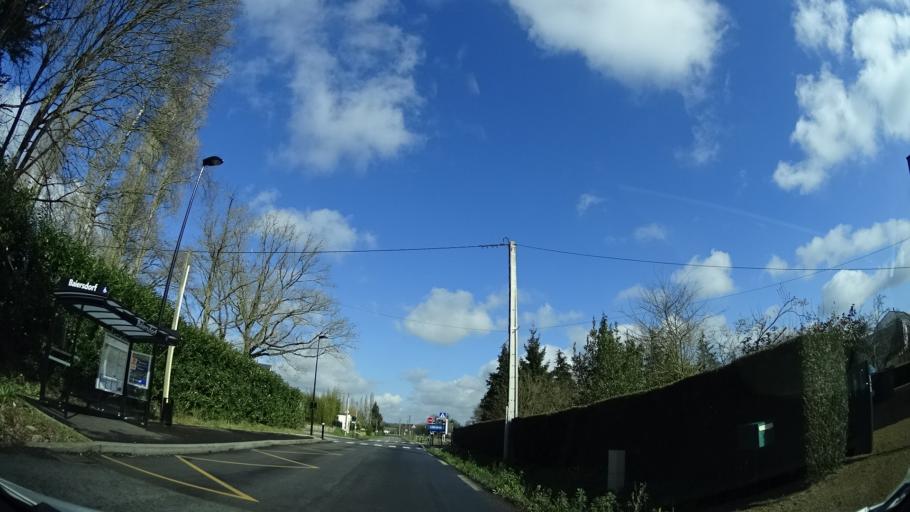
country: FR
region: Brittany
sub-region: Departement d'Ille-et-Vilaine
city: Pace
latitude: 48.1510
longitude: -1.7595
